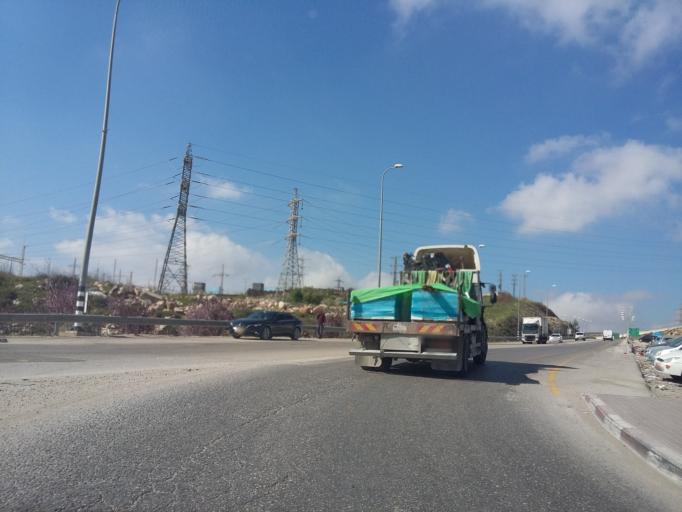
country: PS
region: West Bank
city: Qalandiya
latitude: 31.8601
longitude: 35.2152
